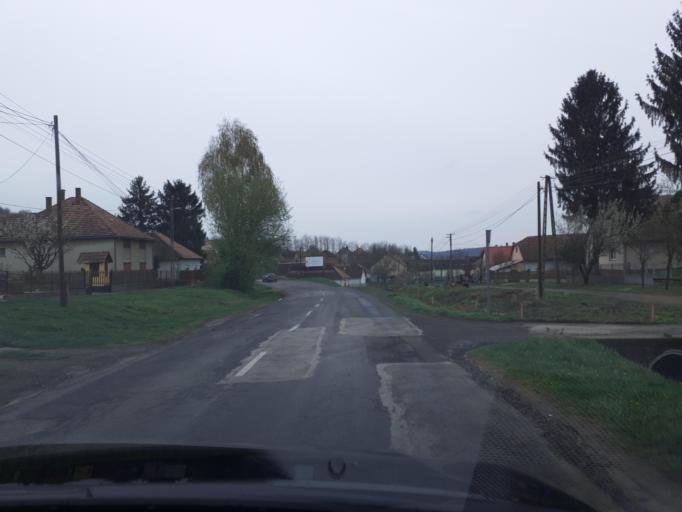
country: HU
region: Tolna
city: Hogyesz
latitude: 46.4238
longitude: 18.4529
